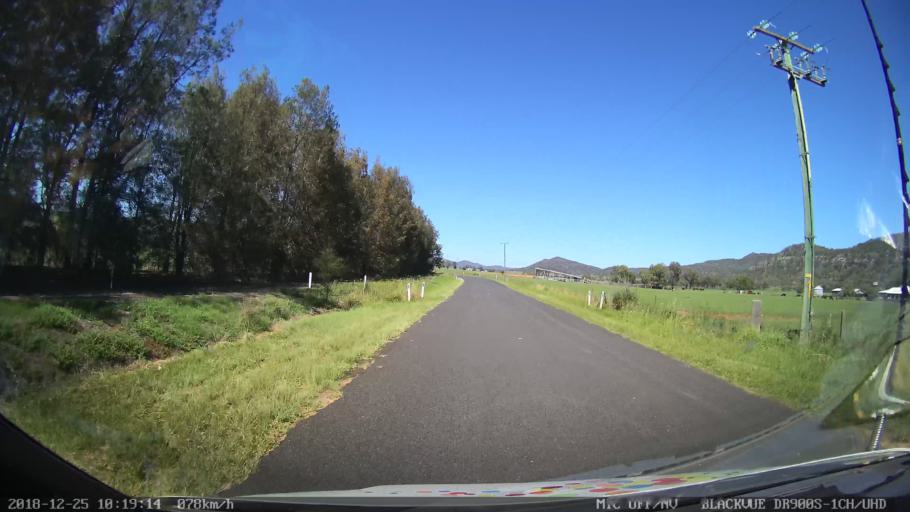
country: AU
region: New South Wales
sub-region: Muswellbrook
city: Denman
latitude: -32.3489
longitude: 150.5603
